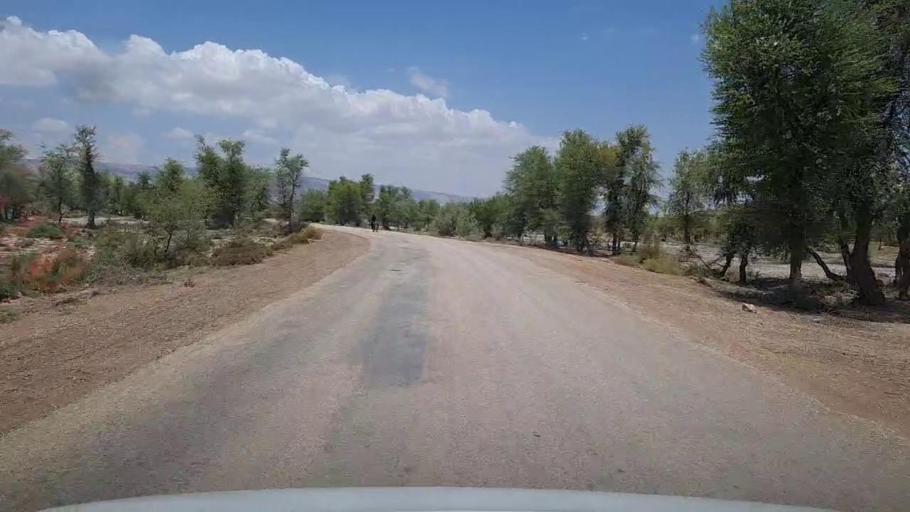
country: PK
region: Sindh
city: Bhan
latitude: 26.3167
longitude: 67.5792
